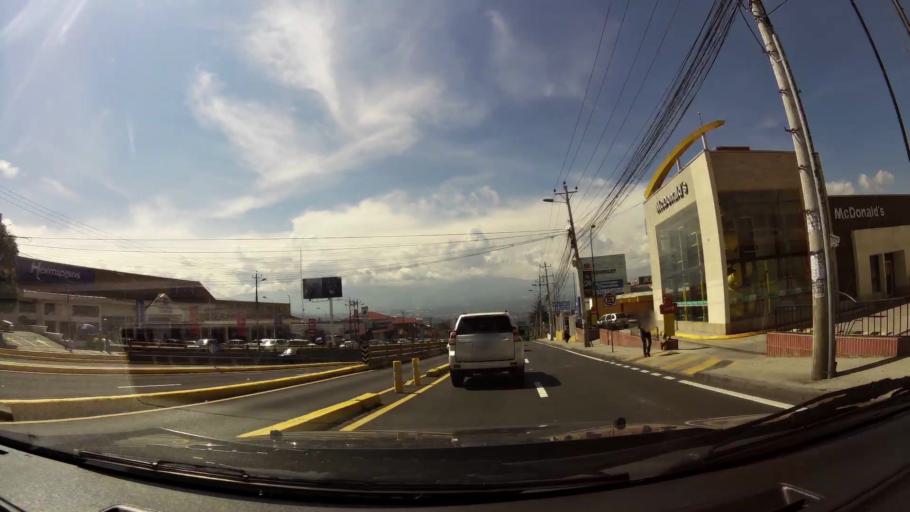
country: EC
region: Pichincha
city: Quito
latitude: -0.1971
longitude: -78.4397
